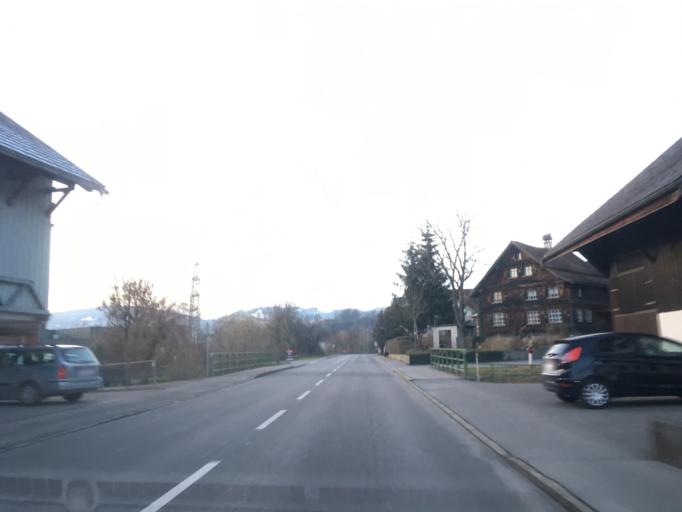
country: AT
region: Vorarlberg
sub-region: Politischer Bezirk Feldkirch
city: Koblach
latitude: 47.3313
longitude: 9.6002
